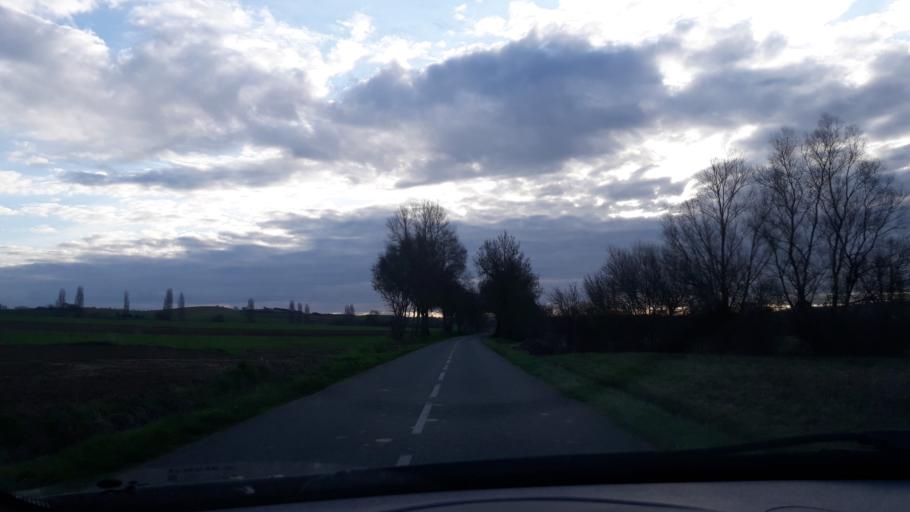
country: FR
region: Midi-Pyrenees
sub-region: Departement du Gers
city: Pujaudran
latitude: 43.6582
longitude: 1.1127
